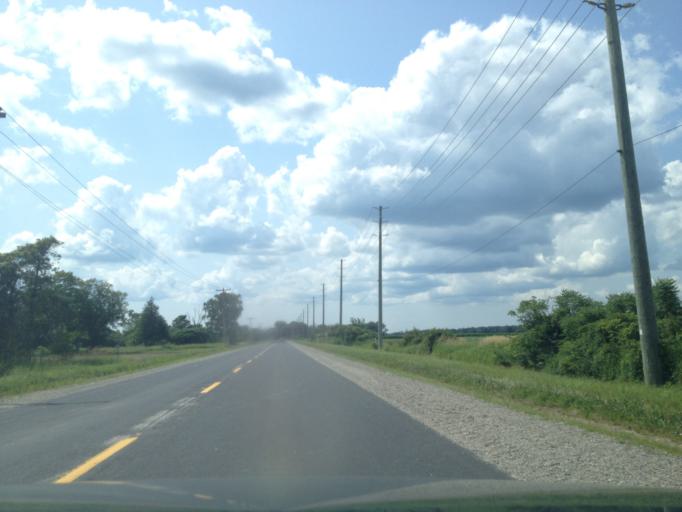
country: CA
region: Ontario
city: Aylmer
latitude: 42.6717
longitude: -80.8513
